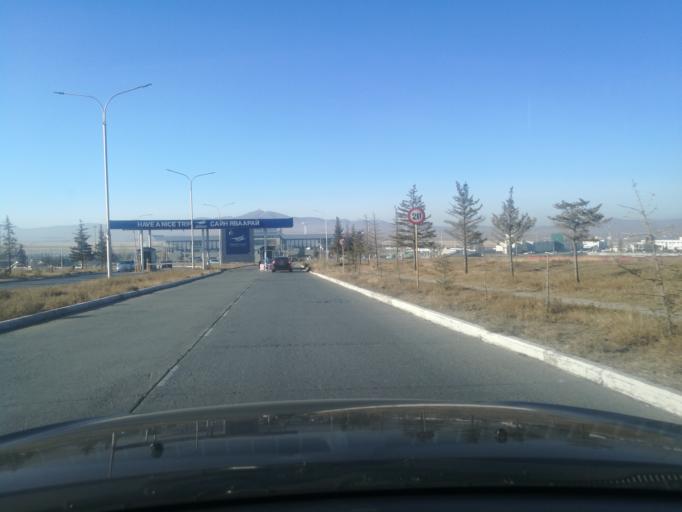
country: MN
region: Ulaanbaatar
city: Ulaanbaatar
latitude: 47.8553
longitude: 106.7668
